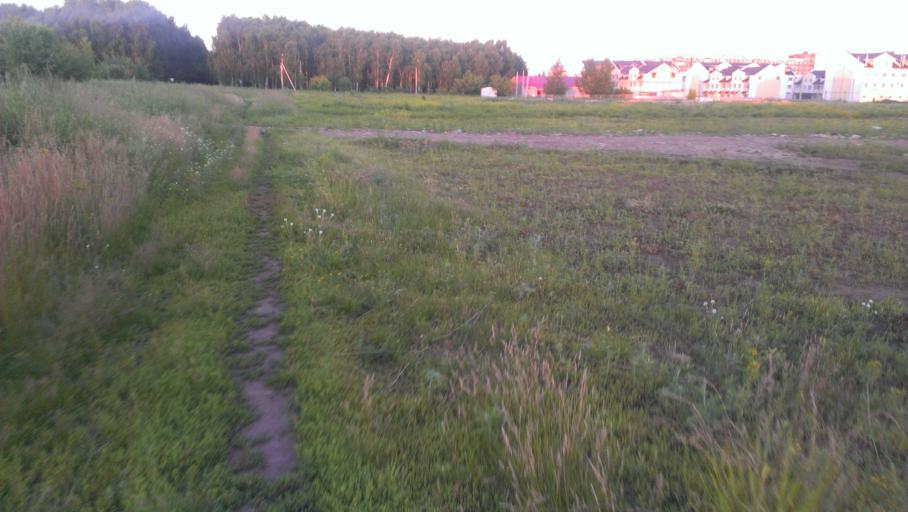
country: RU
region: Altai Krai
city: Novosilikatnyy
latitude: 53.3636
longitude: 83.6542
